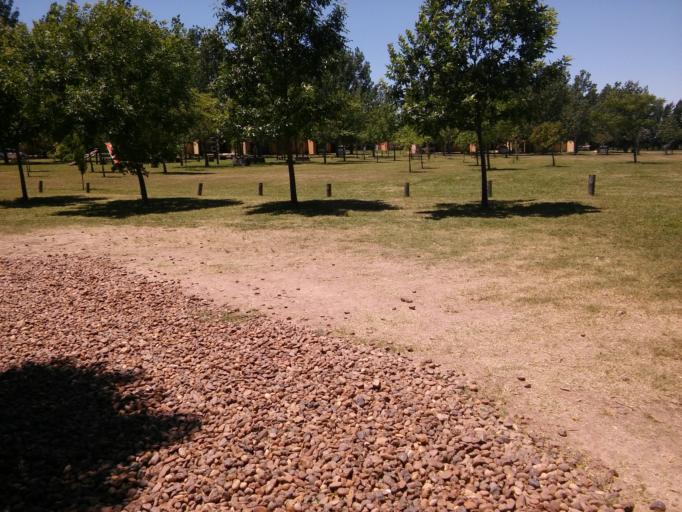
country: AR
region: Entre Rios
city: Concepcion del Uruguay
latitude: -32.4512
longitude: -58.2902
